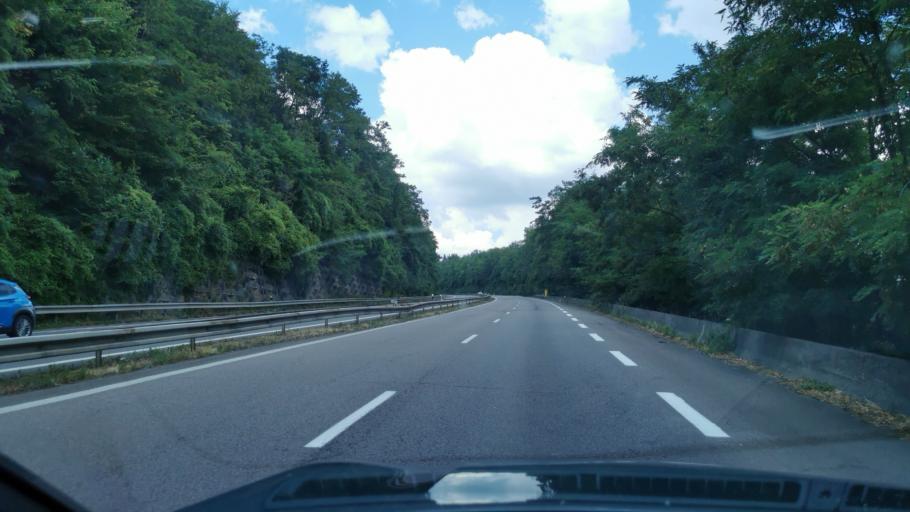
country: FR
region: Lorraine
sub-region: Departement de Meurthe-et-Moselle
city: Crusnes
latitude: 49.4295
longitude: 5.9099
